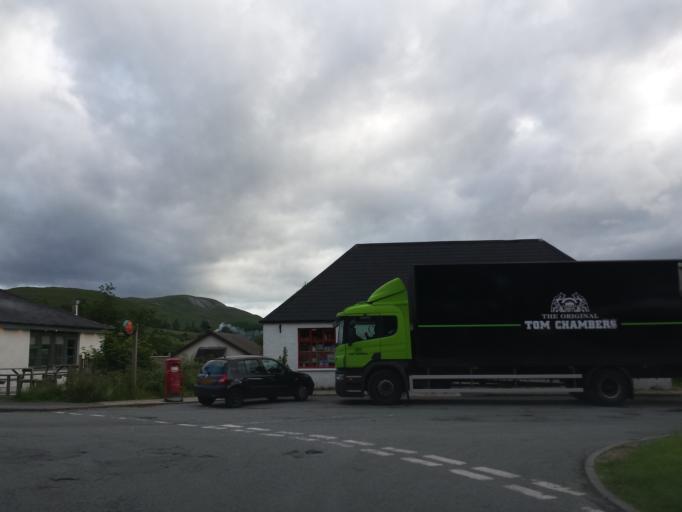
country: GB
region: Scotland
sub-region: Highland
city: Portree
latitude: 57.2433
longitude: -5.9148
